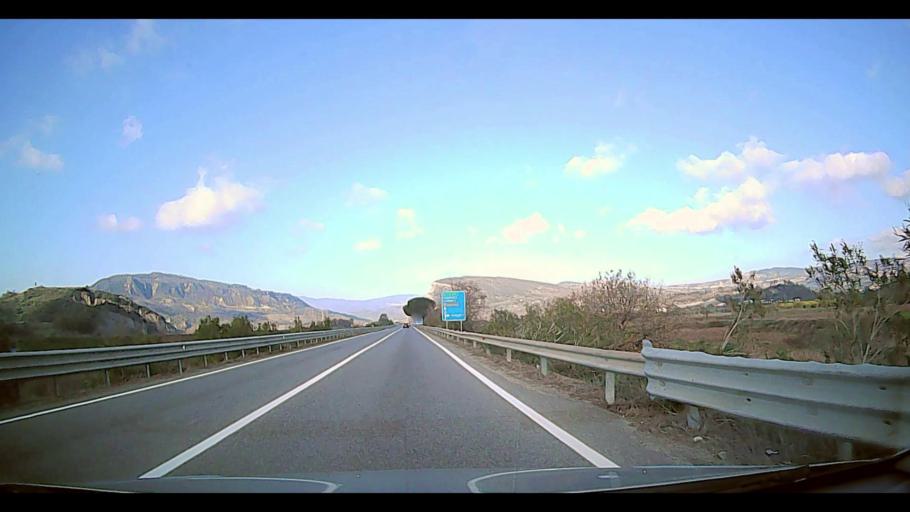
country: IT
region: Calabria
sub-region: Provincia di Crotone
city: Santa Severina
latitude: 39.1779
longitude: 16.9258
